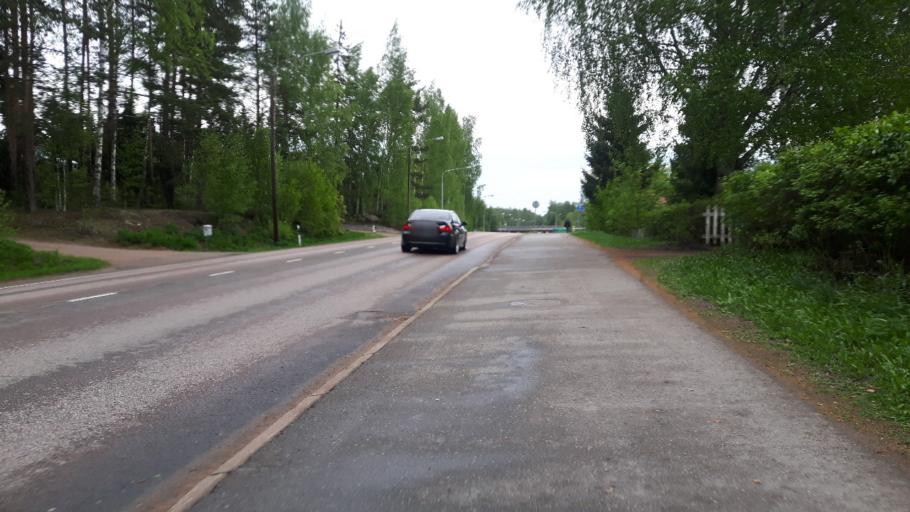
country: FI
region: Kymenlaakso
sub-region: Kotka-Hamina
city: Hamina
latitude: 60.5638
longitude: 27.1543
